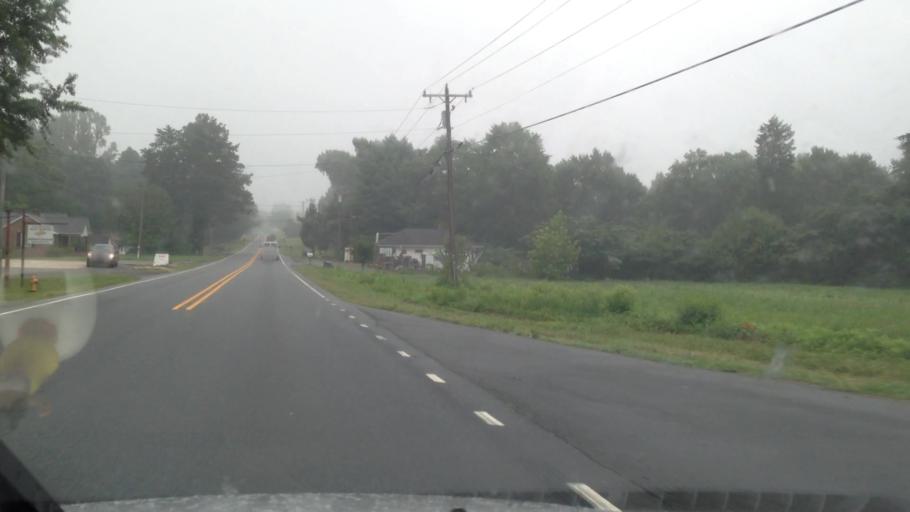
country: US
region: North Carolina
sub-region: Forsyth County
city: Walkertown
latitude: 36.1577
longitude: -80.1307
